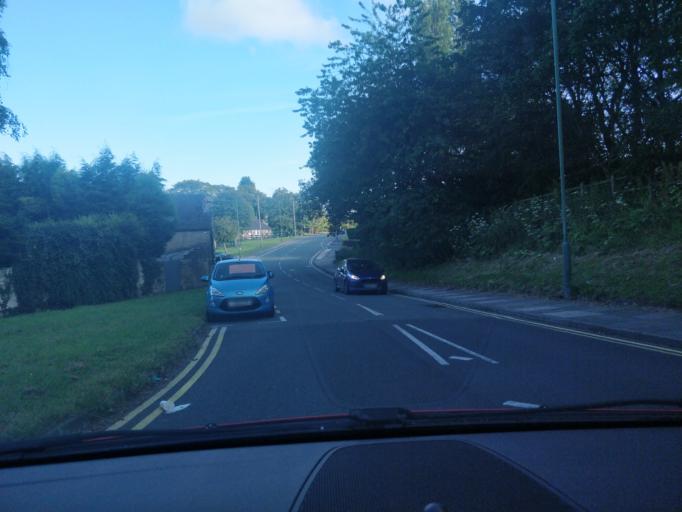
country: GB
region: England
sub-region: St. Helens
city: Billinge
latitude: 53.5342
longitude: -2.7190
